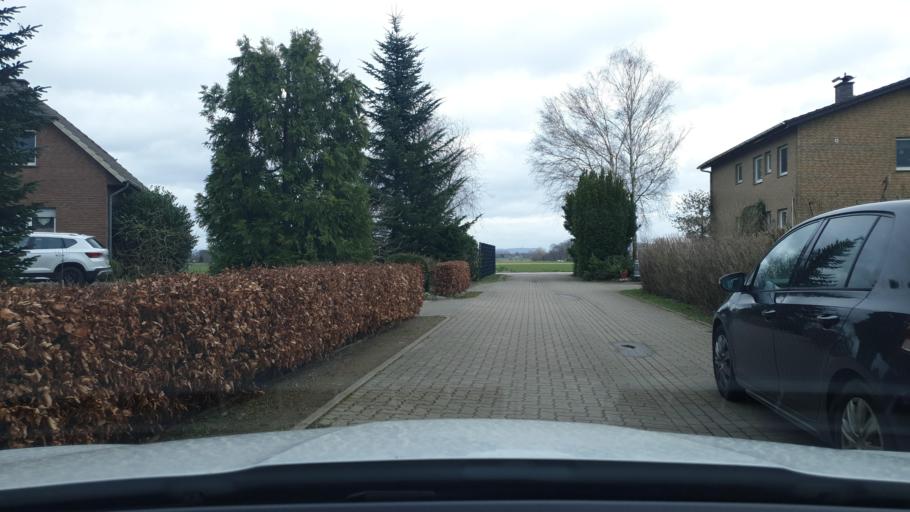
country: DE
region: North Rhine-Westphalia
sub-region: Regierungsbezirk Detmold
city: Hille
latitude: 52.3315
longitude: 8.7501
